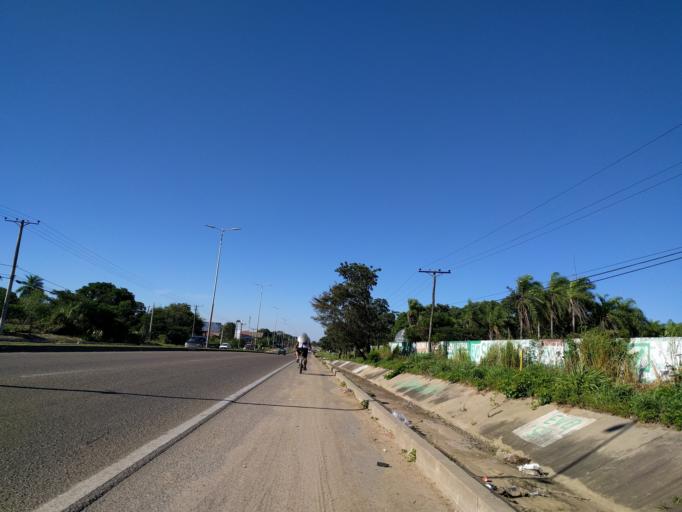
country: BO
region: Santa Cruz
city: Santa Cruz de la Sierra
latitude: -17.8570
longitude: -63.2592
